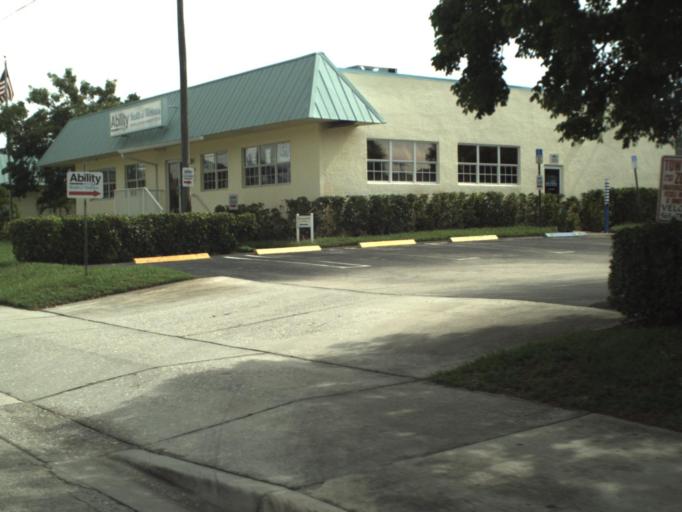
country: US
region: Florida
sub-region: Palm Beach County
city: Delray Beach
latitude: 26.4582
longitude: -80.0935
